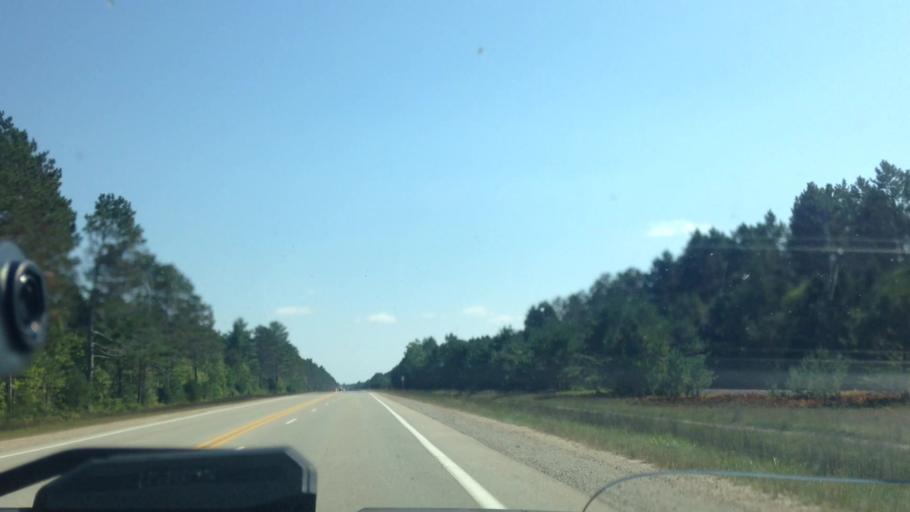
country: US
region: Michigan
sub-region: Alger County
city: Munising
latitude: 46.3653
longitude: -86.5313
